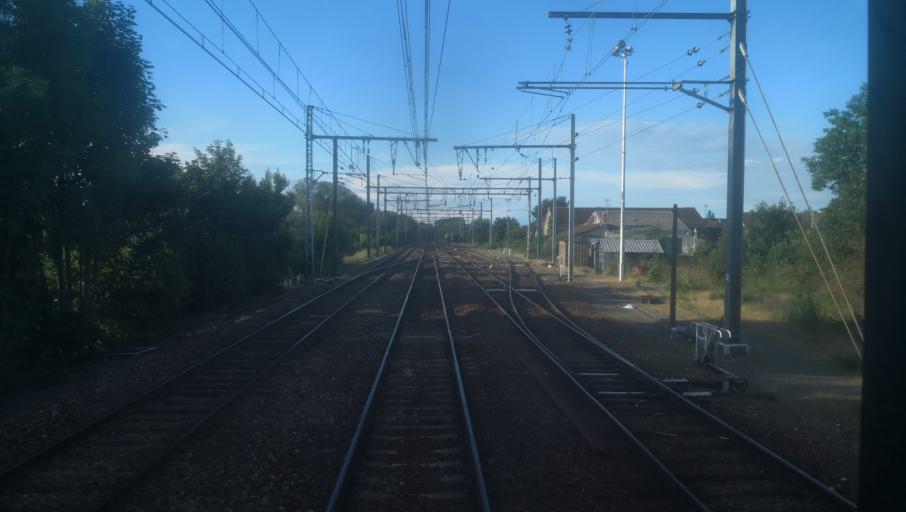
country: FR
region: Centre
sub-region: Departement de l'Indre
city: Issoudun
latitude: 46.9504
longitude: 1.9866
